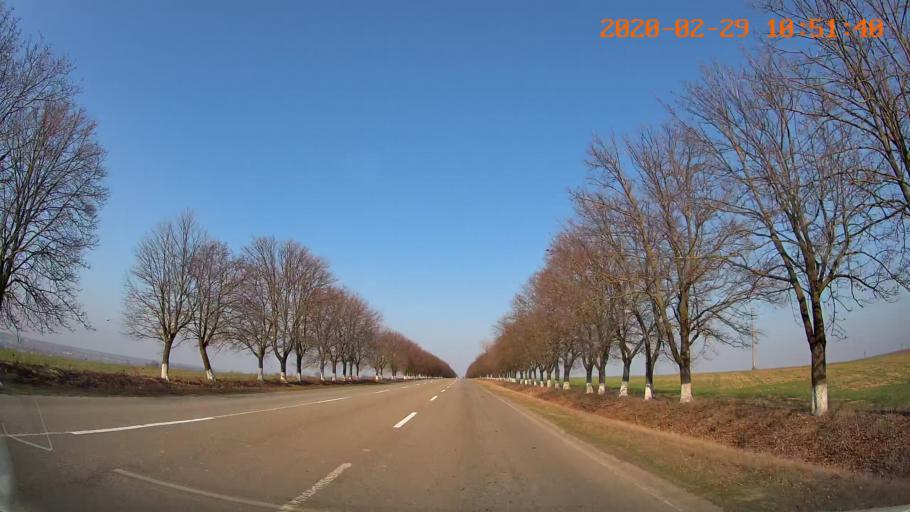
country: MD
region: Telenesti
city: Grigoriopol
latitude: 47.0958
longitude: 29.3611
